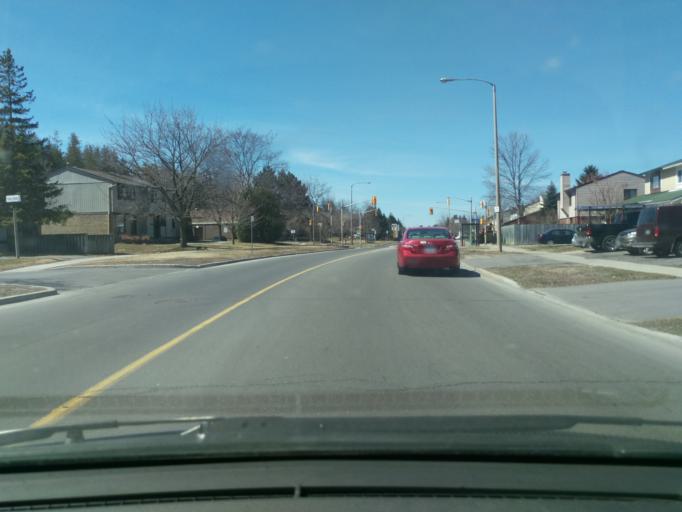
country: CA
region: Quebec
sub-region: Outaouais
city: Gatineau
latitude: 45.4824
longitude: -75.5259
